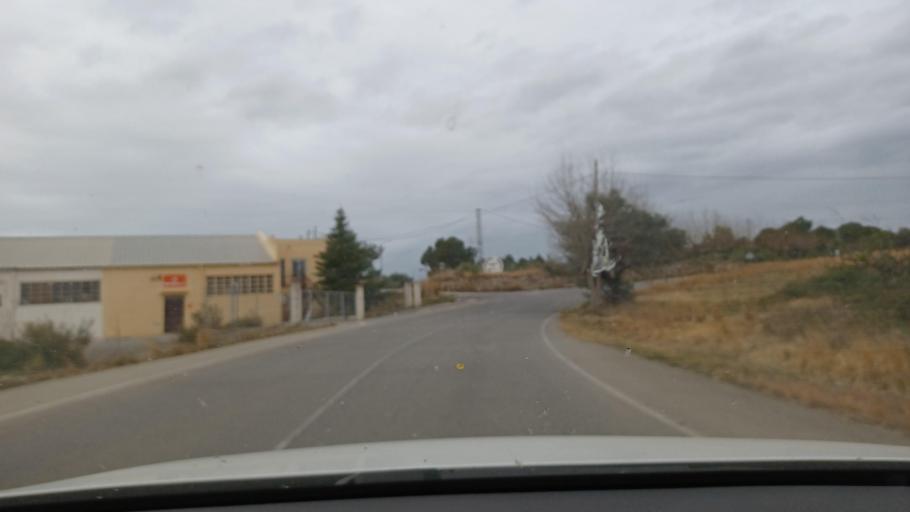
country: ES
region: Valencia
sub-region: Provincia de Castello
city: Rosell
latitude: 40.6298
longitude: 0.2908
